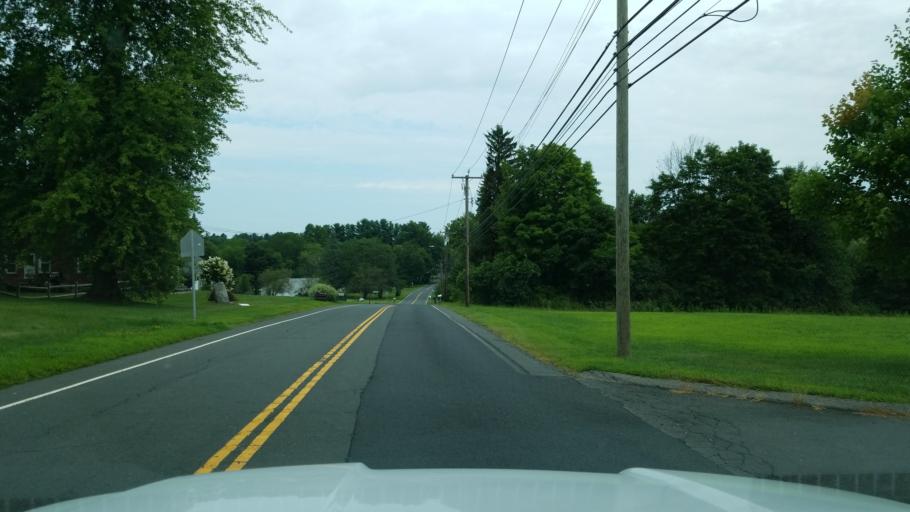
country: US
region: Connecticut
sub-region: Hartford County
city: Blue Hills
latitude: 41.8389
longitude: -72.7464
